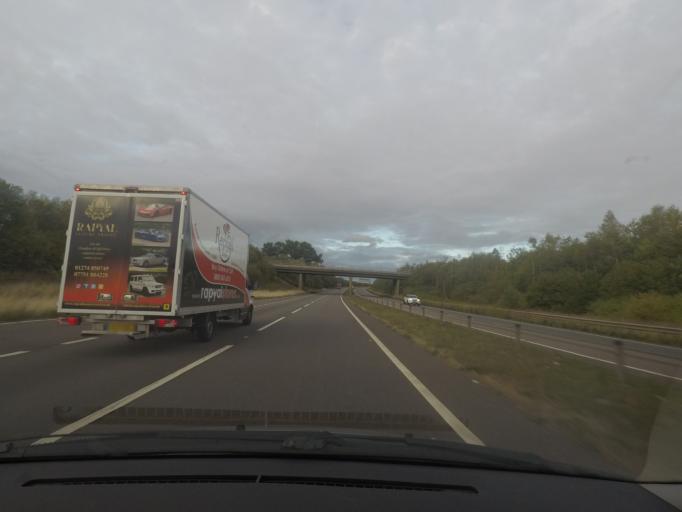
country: GB
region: England
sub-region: Northamptonshire
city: Brackley
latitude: 51.9732
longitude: -1.1910
